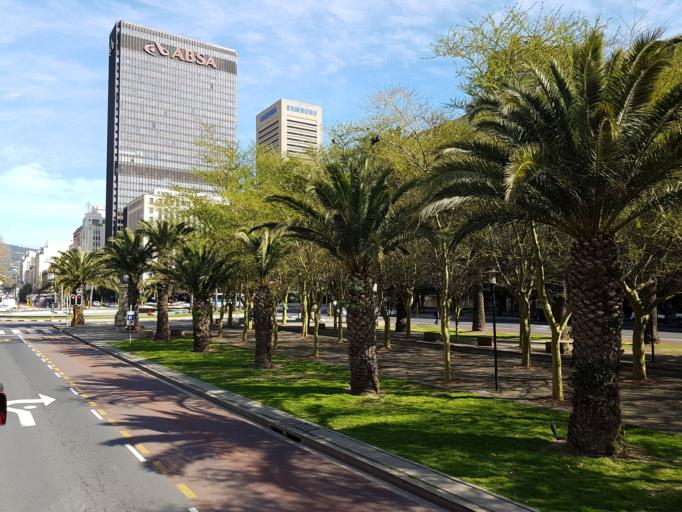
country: ZA
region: Western Cape
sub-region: City of Cape Town
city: Cape Town
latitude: -33.9192
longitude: 18.4266
